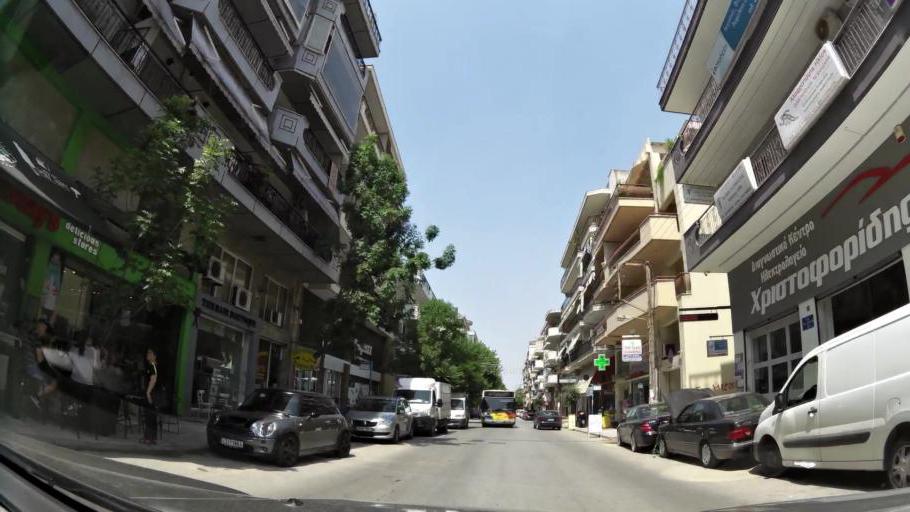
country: GR
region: Central Macedonia
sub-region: Nomos Thessalonikis
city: Evosmos
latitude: 40.6703
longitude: 22.9045
